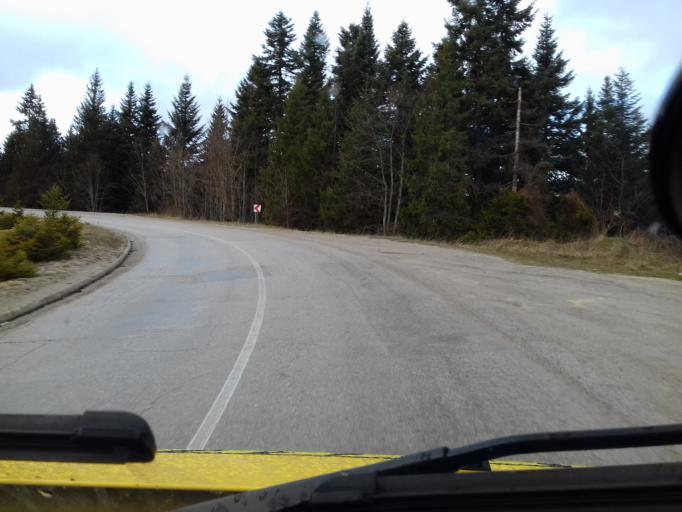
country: BA
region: Federation of Bosnia and Herzegovina
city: Turbe
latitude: 44.3091
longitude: 17.4919
